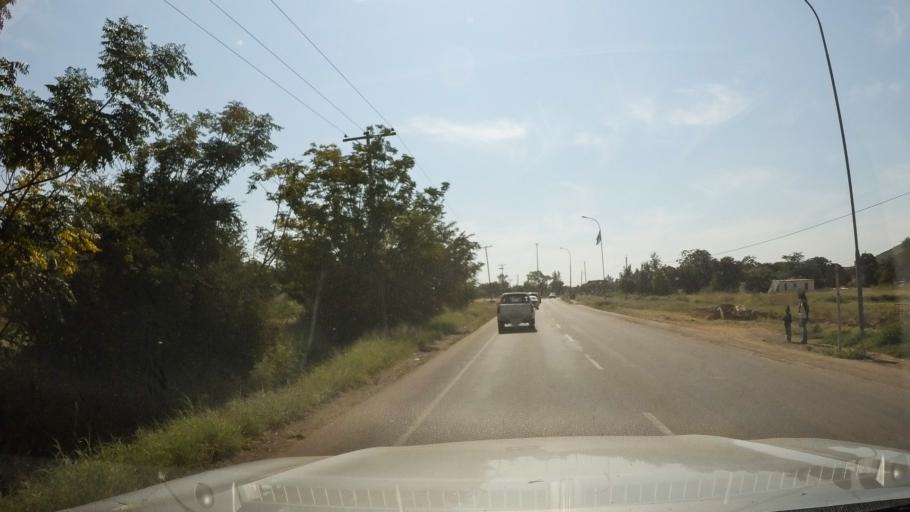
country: BW
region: South East
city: Lobatse
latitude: -25.2156
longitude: 25.6815
